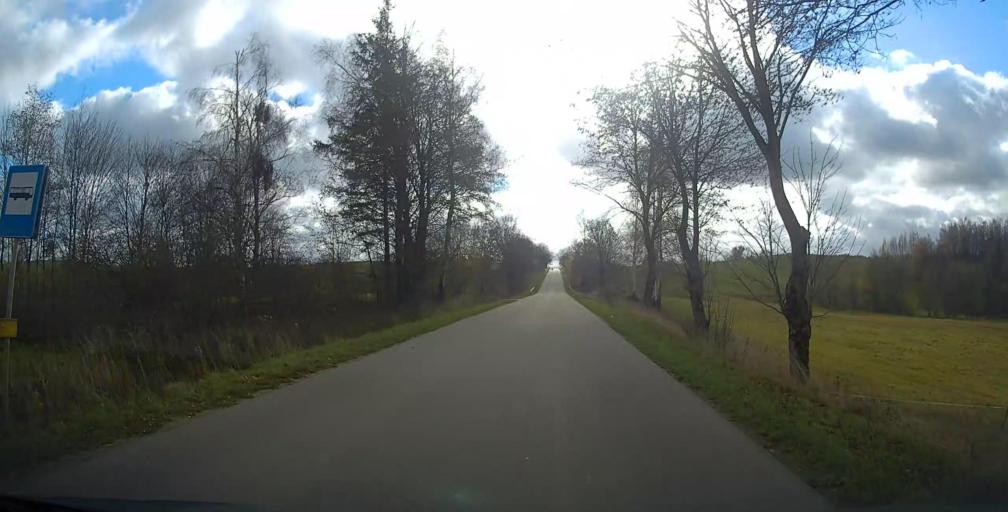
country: PL
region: Podlasie
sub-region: Suwalki
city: Suwalki
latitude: 54.3225
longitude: 22.8627
